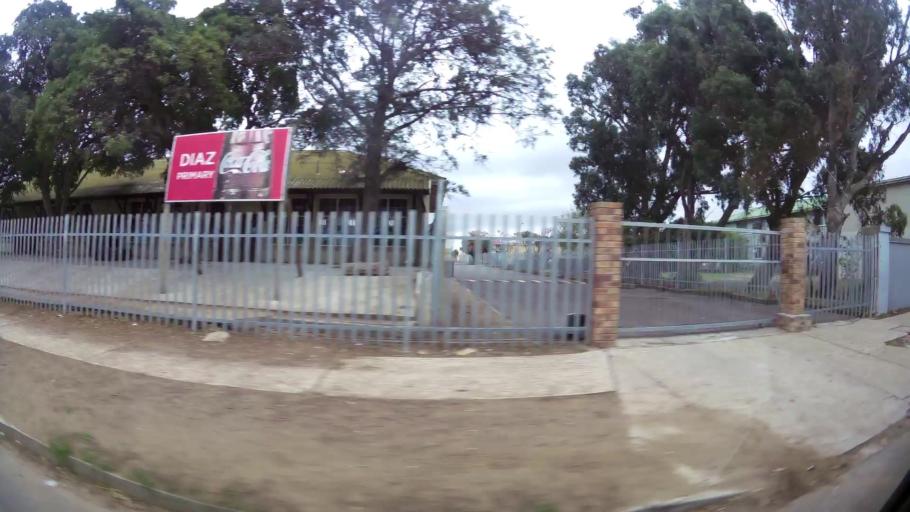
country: ZA
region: Eastern Cape
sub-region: Nelson Mandela Bay Metropolitan Municipality
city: Port Elizabeth
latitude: -33.9062
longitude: 25.5678
